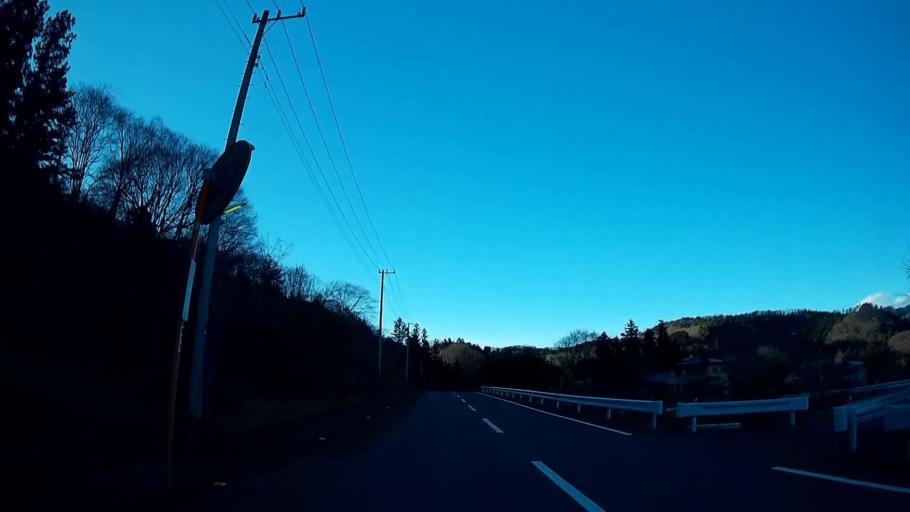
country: JP
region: Saitama
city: Chichibu
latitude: 36.0370
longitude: 139.0134
